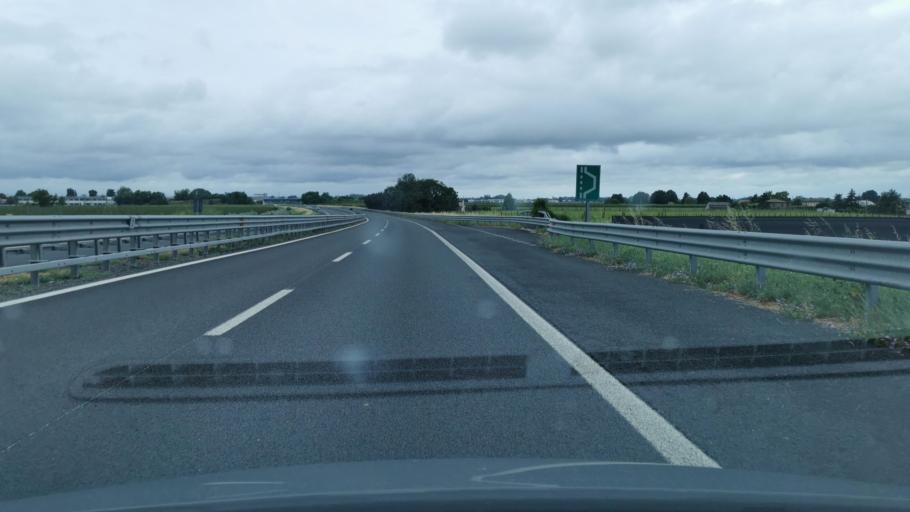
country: IT
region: Emilia-Romagna
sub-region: Provincia di Ravenna
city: Russi
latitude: 44.4071
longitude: 12.0199
